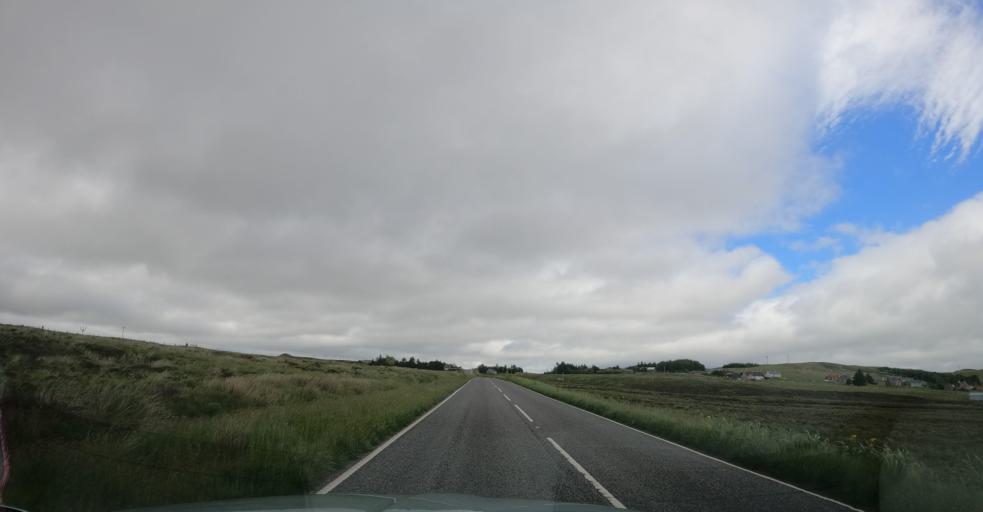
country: GB
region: Scotland
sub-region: Eilean Siar
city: Stornoway
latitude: 58.1480
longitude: -6.5059
